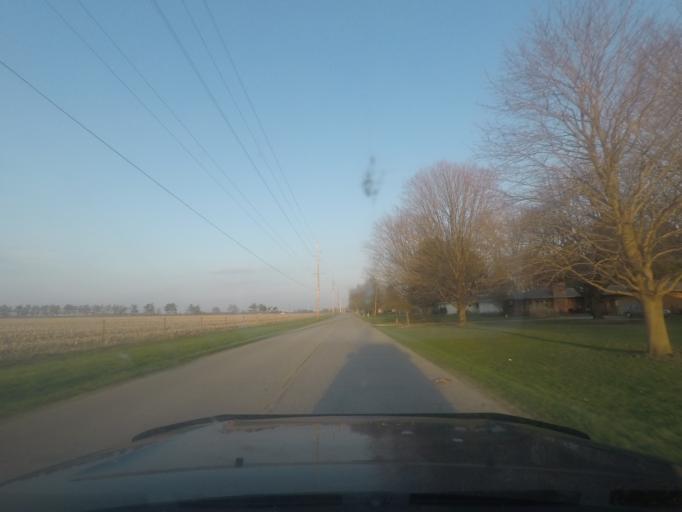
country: US
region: Indiana
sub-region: LaPorte County
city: LaPorte
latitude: 41.5691
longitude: -86.7051
